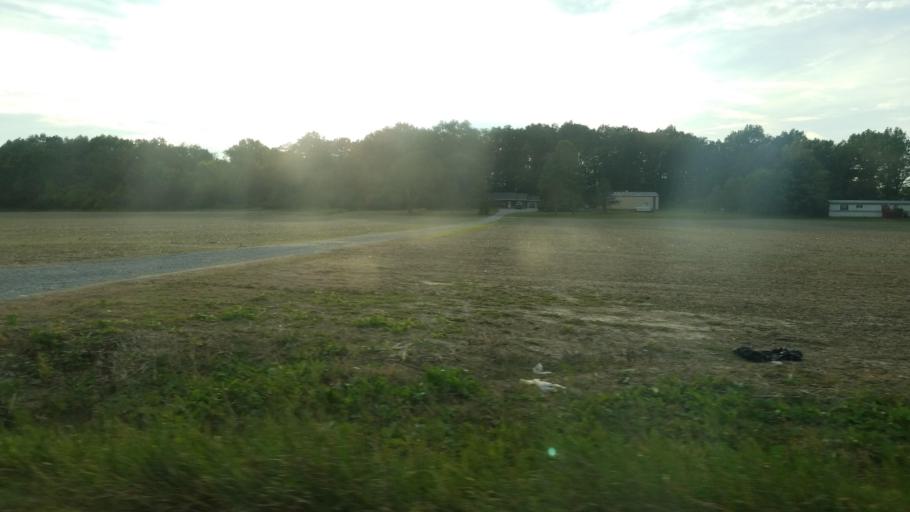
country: US
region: Illinois
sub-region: Saline County
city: Harrisburg
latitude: 37.7929
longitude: -88.5400
